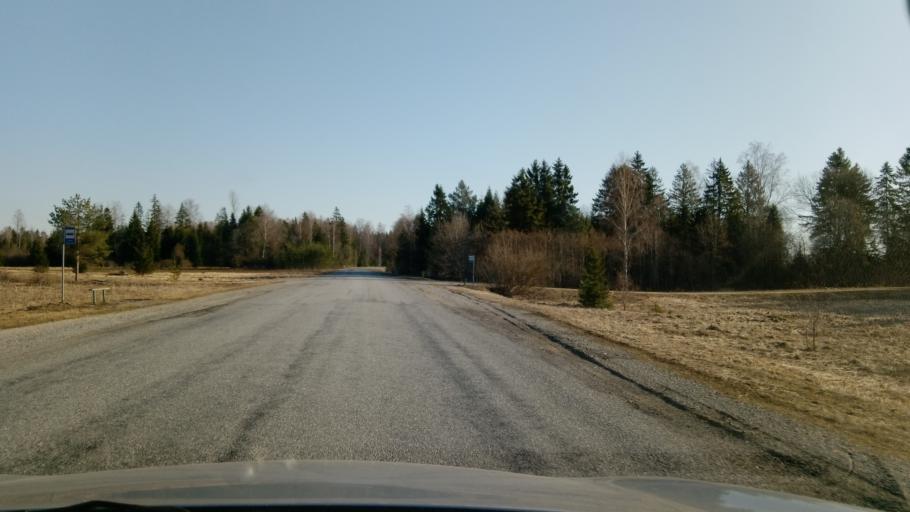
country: EE
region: Jaervamaa
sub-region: Jaerva-Jaani vald
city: Jarva-Jaani
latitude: 59.0500
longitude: 25.9096
